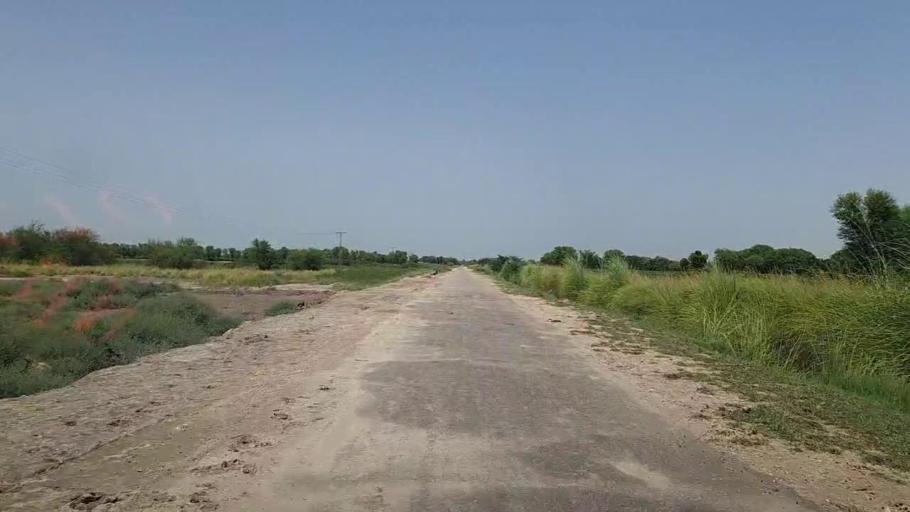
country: PK
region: Sindh
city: Pad Idan
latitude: 26.7474
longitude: 68.3149
